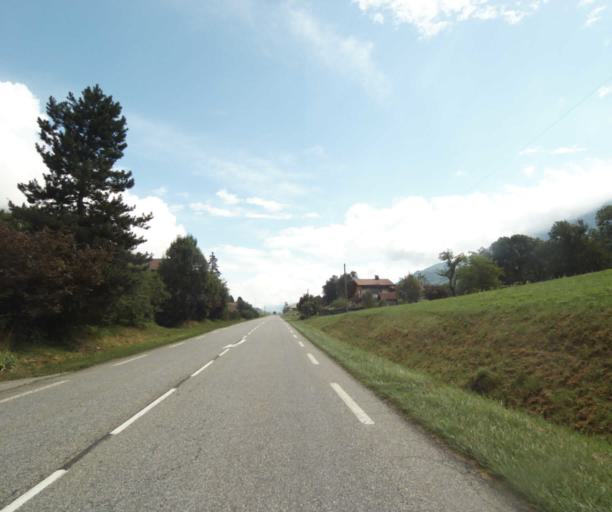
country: FR
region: Rhone-Alpes
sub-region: Departement de la Haute-Savoie
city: Thones
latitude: 45.9000
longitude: 6.3507
